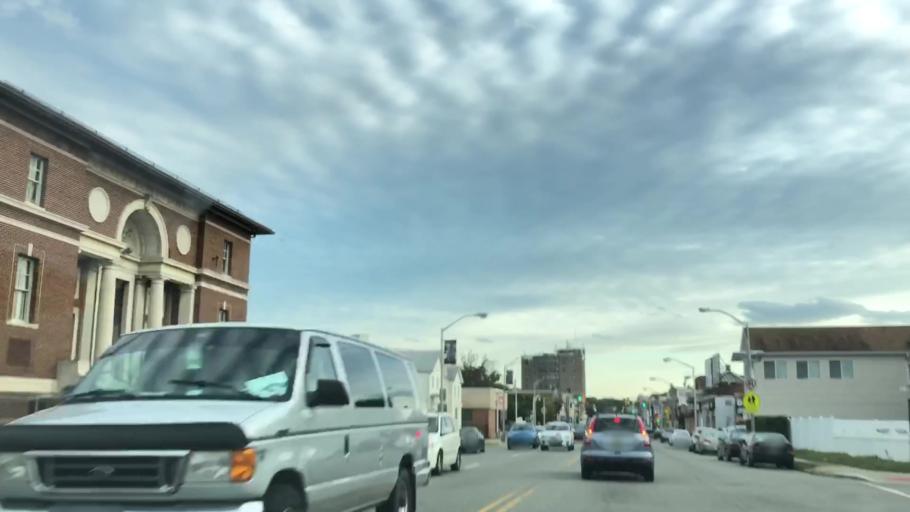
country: US
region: New Jersey
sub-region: Essex County
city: Glen Ridge
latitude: 40.7970
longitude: -74.2003
